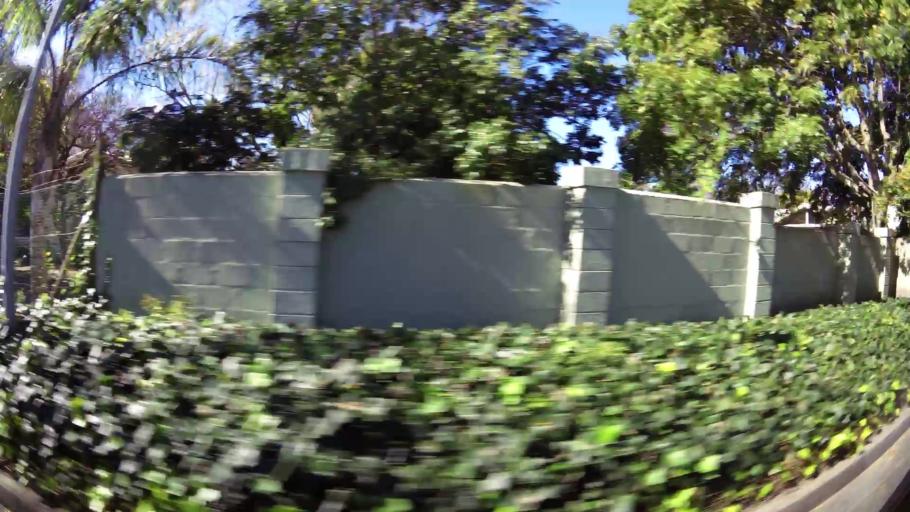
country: ZA
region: Western Cape
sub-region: Eden District Municipality
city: George
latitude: -33.9482
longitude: 22.4587
